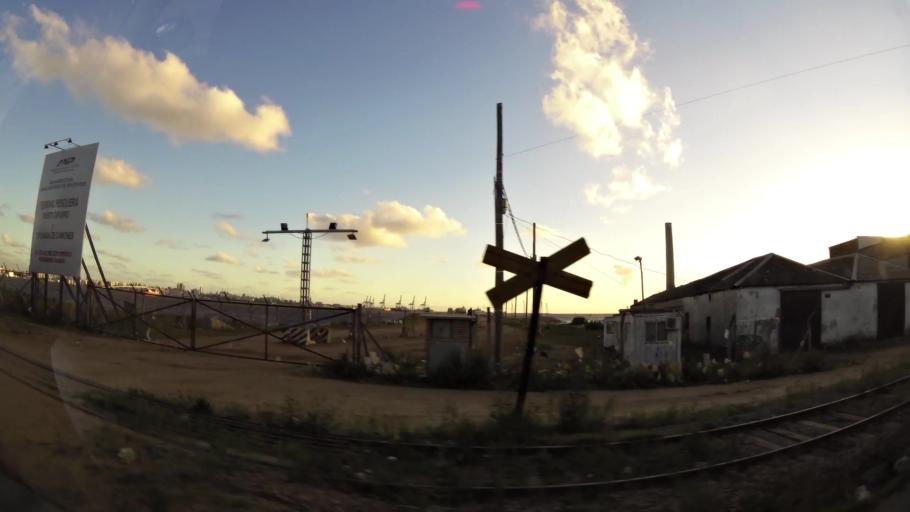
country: UY
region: Montevideo
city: Montevideo
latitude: -34.8733
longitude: -56.2180
